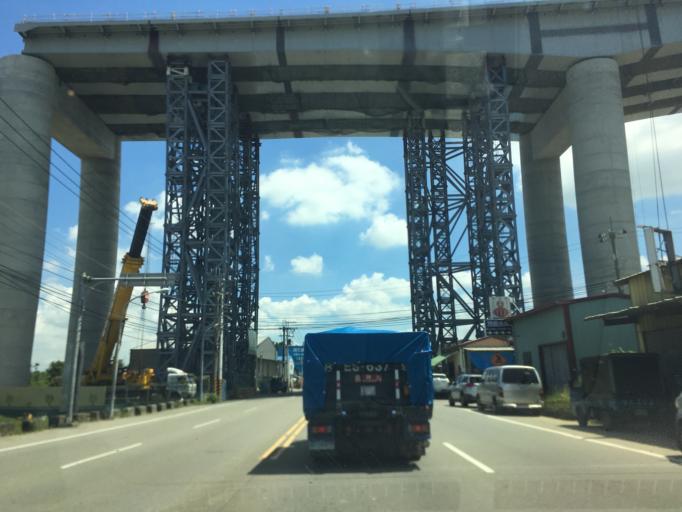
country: TW
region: Taiwan
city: Fengyuan
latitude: 24.2202
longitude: 120.7239
